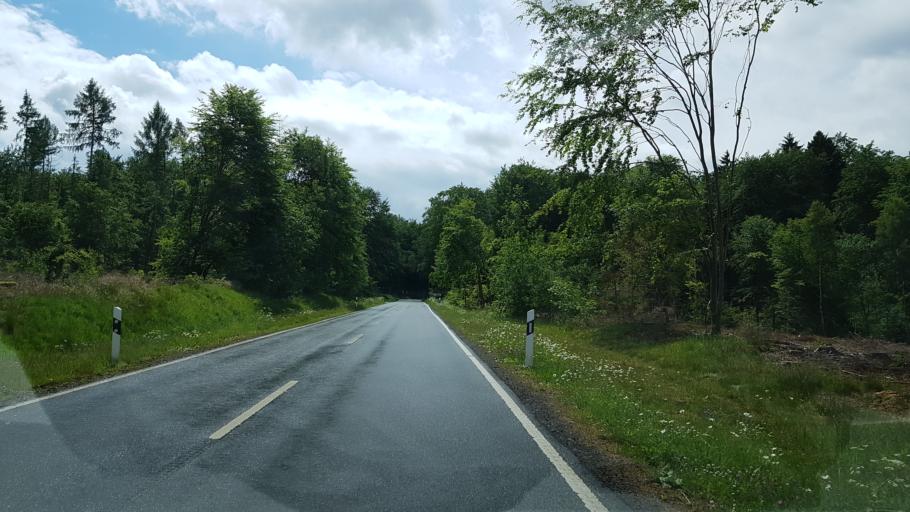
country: DE
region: Lower Saxony
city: Bodenfelde
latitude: 51.5933
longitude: 9.5212
